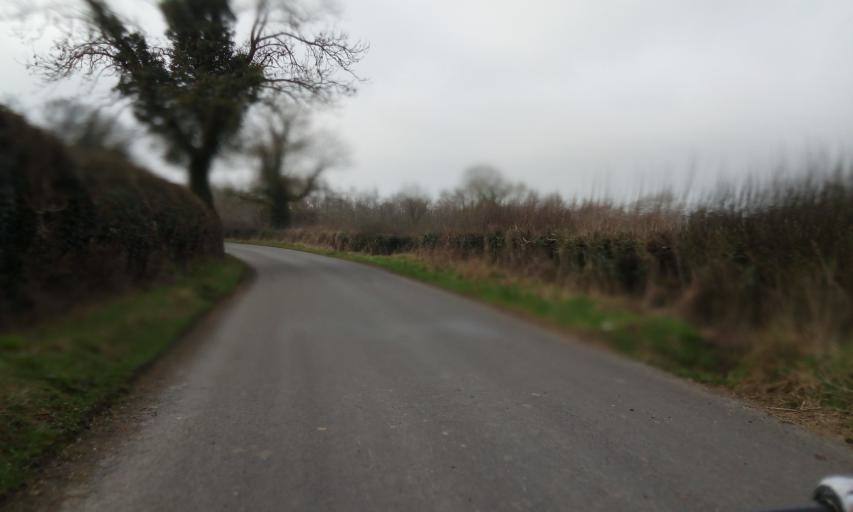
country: IE
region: Leinster
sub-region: Kilkenny
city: Kilkenny
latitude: 52.6635
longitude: -7.1877
